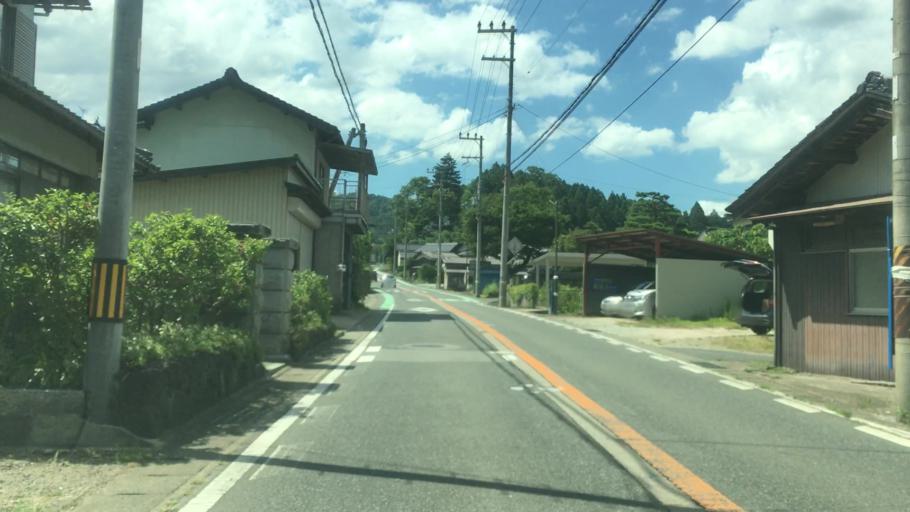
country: JP
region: Hyogo
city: Toyooka
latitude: 35.4730
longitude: 134.7159
